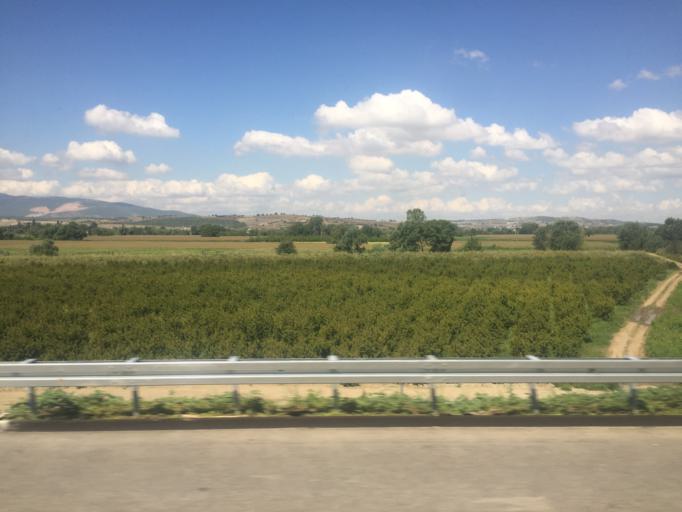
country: TR
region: Balikesir
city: Gobel
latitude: 39.9997
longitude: 28.1928
